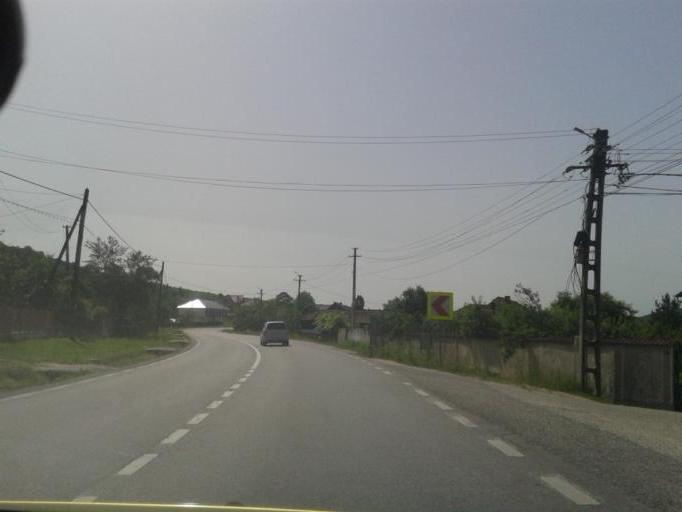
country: RO
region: Arges
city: Draganu-Olteni
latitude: 44.9379
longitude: 24.7059
